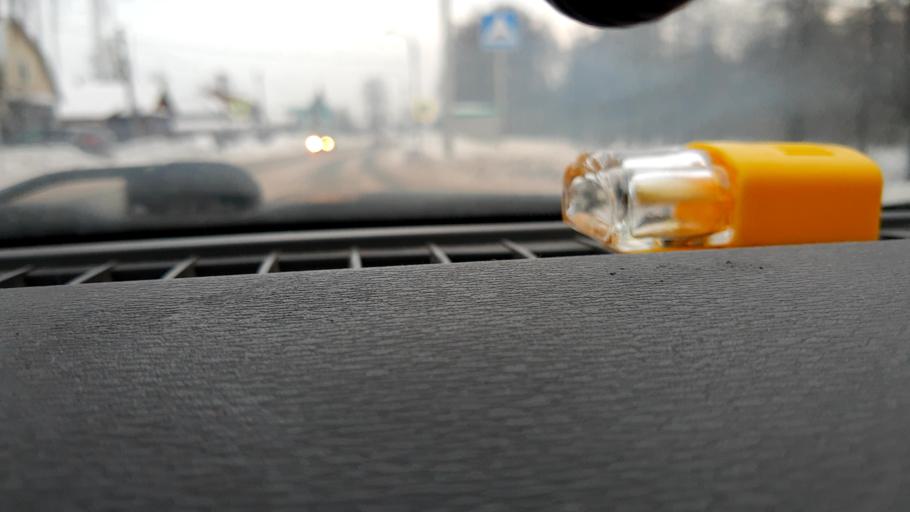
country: RU
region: Bashkortostan
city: Ufa
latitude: 54.8118
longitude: 56.1637
